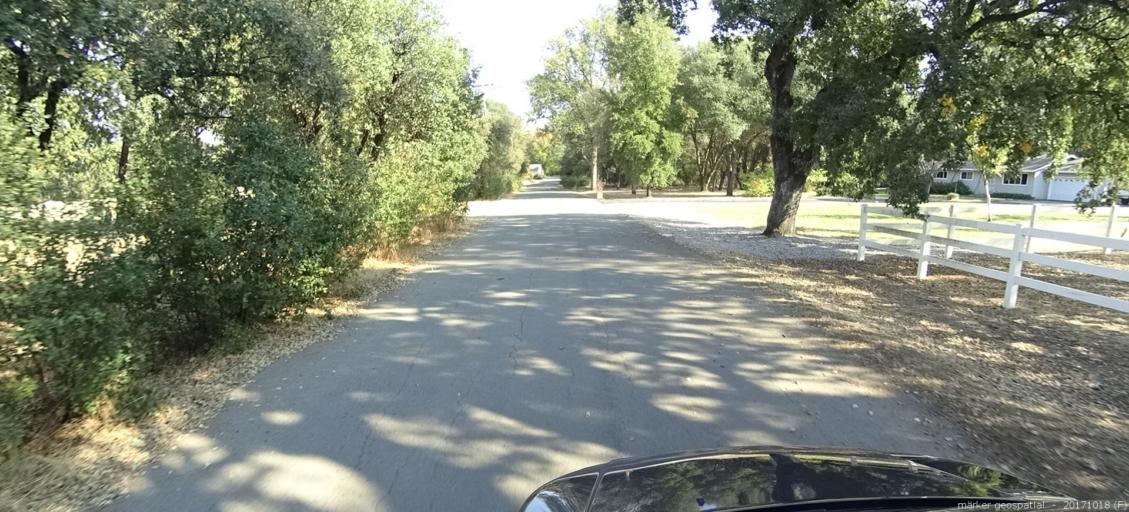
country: US
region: California
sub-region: Shasta County
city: Palo Cedro
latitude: 40.5768
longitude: -122.2307
